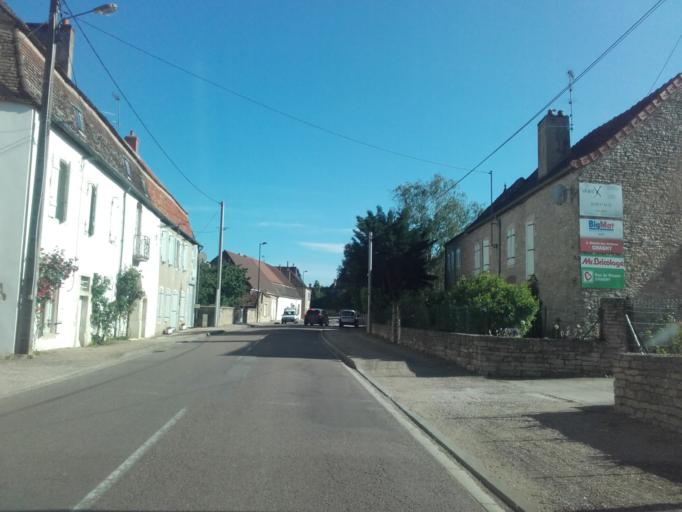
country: FR
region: Bourgogne
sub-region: Departement de Saone-et-Loire
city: Demigny
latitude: 46.9320
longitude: 4.8329
